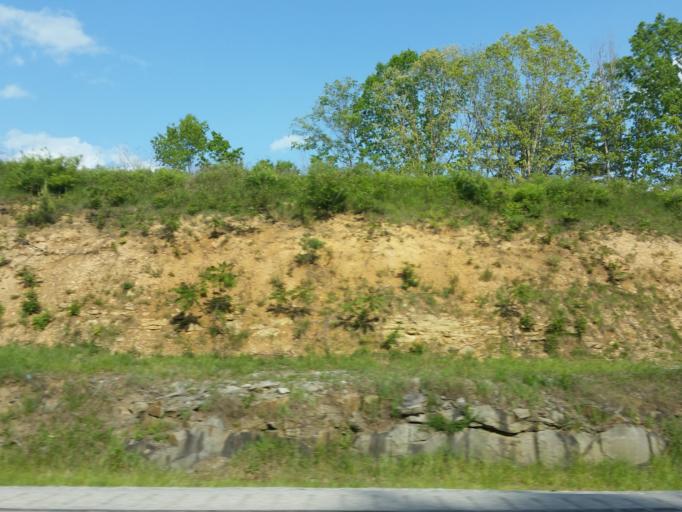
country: US
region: West Virginia
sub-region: Mercer County
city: Athens
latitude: 37.4550
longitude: -81.0652
